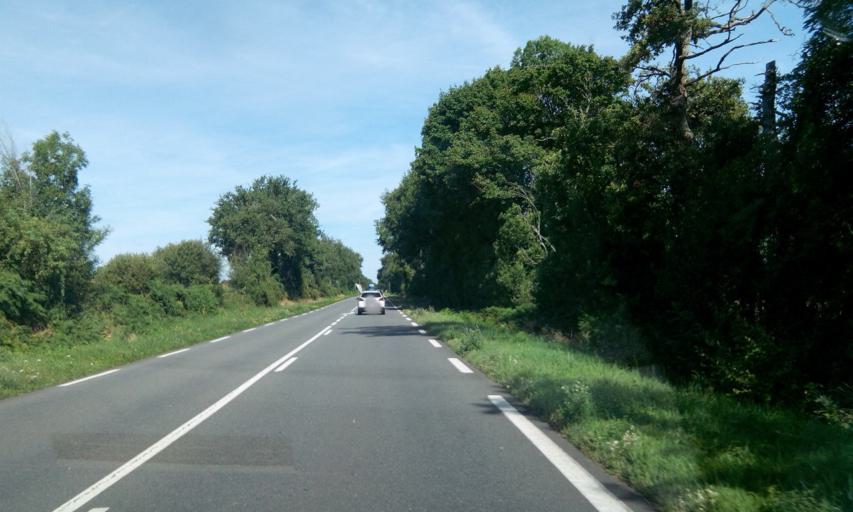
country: FR
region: Poitou-Charentes
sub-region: Departement de la Charente
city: Confolens
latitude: 46.0330
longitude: 0.6400
